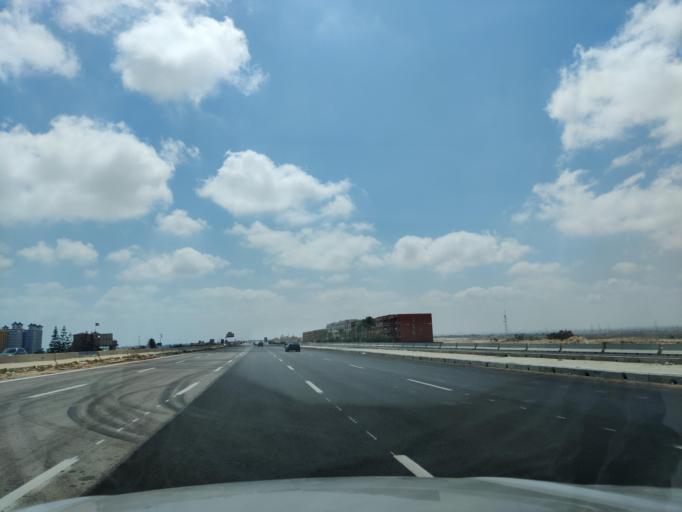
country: EG
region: Muhafazat Matruh
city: Al `Alamayn
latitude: 30.8224
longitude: 28.9958
